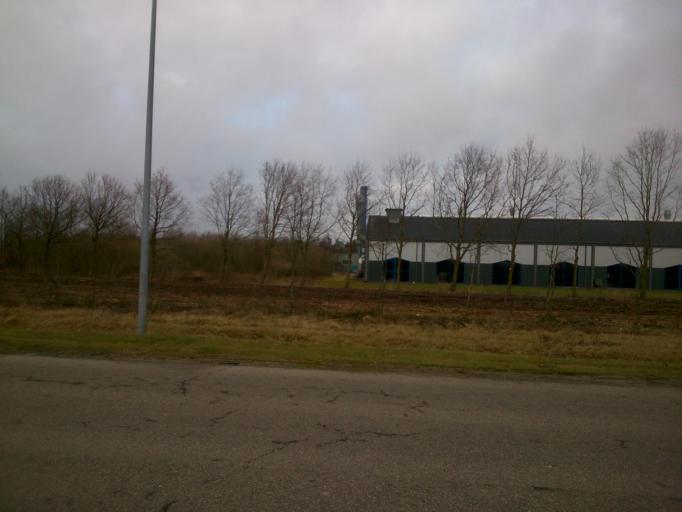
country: DK
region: Central Jutland
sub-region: Ringkobing-Skjern Kommune
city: Skjern
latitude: 55.9651
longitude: 8.4954
